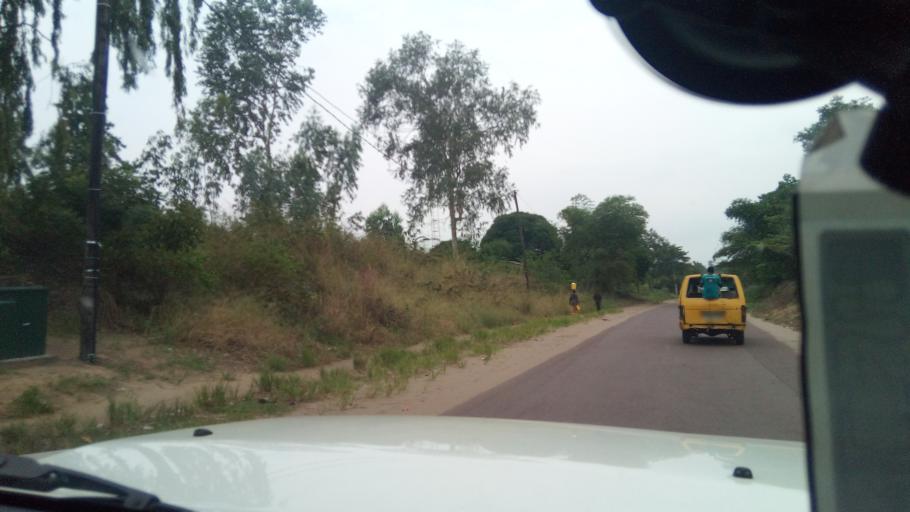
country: CD
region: Kinshasa
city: Masina
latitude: -4.1914
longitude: 15.5524
